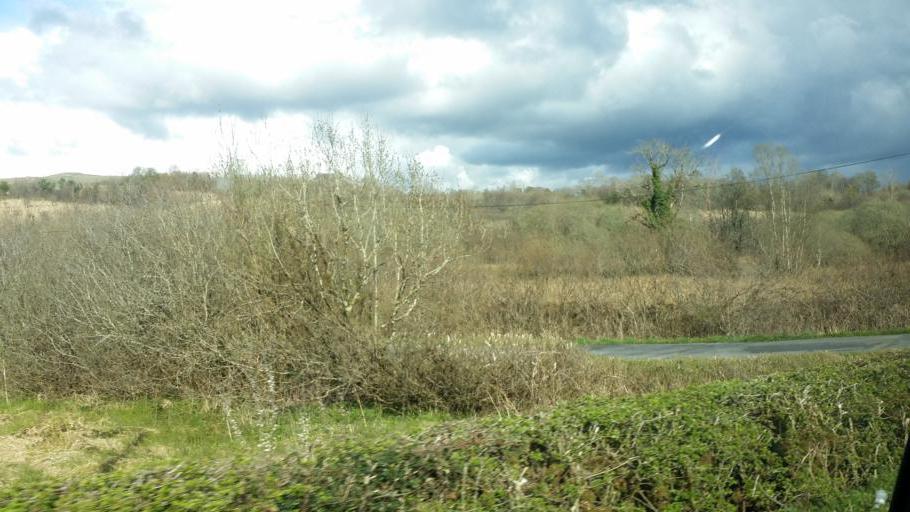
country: IE
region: Connaught
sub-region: County Leitrim
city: Manorhamilton
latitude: 54.3299
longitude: -8.2107
